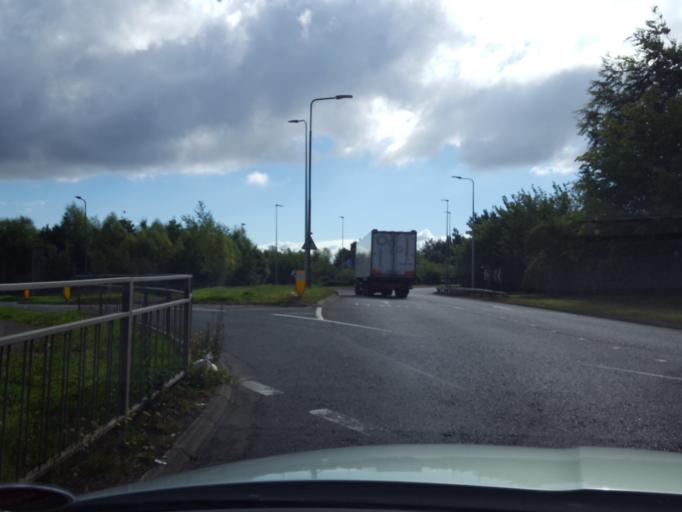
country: GB
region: Scotland
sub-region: Fife
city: Rosyth
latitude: 56.0479
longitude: -3.4295
